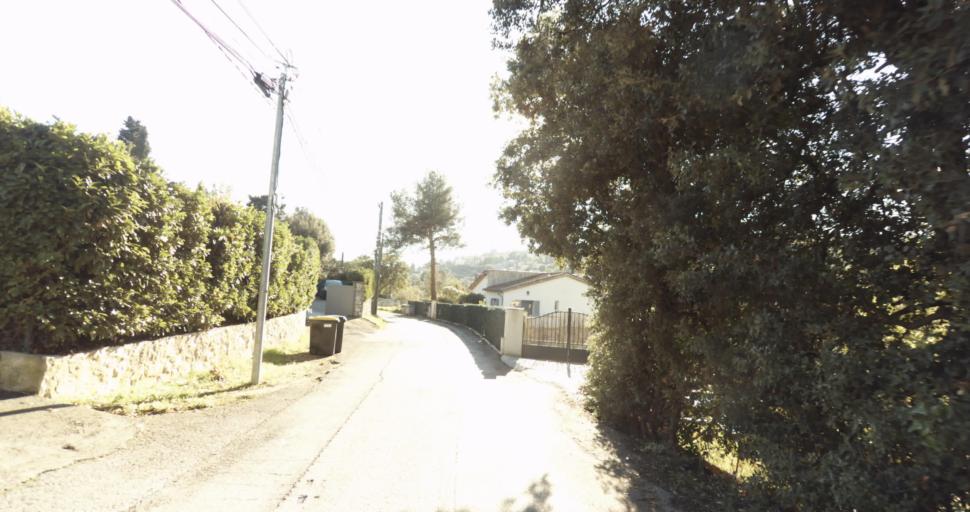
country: FR
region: Provence-Alpes-Cote d'Azur
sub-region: Departement des Alpes-Maritimes
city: Vence
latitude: 43.7256
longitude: 7.1292
